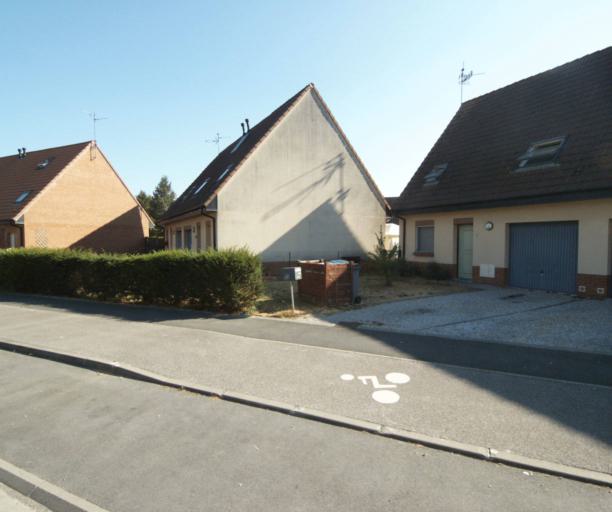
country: FR
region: Nord-Pas-de-Calais
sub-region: Departement du Nord
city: Wervicq-Sud
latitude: 50.7735
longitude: 3.0473
